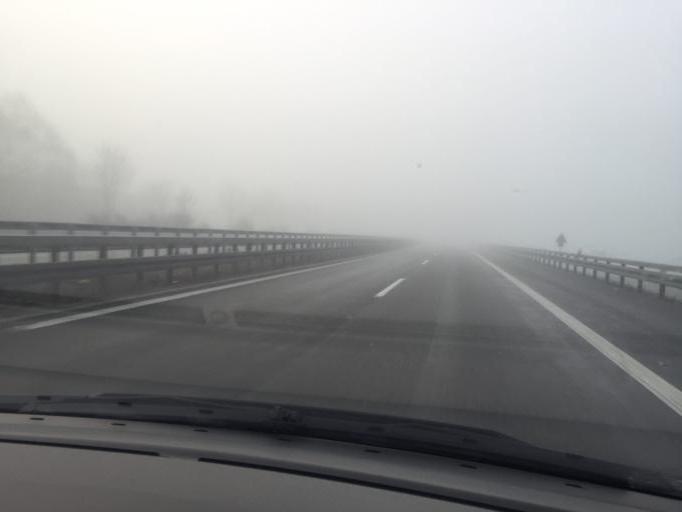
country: DE
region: Baden-Wuerttemberg
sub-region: Freiburg Region
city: Donaueschingen
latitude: 47.9753
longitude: 8.5144
